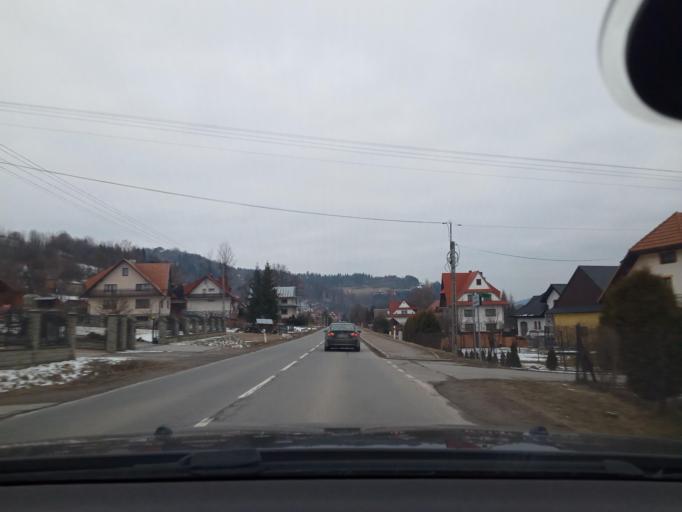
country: PL
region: Lesser Poland Voivodeship
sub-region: Powiat limanowski
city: Mszana Gorna
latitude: 49.6391
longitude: 20.1267
